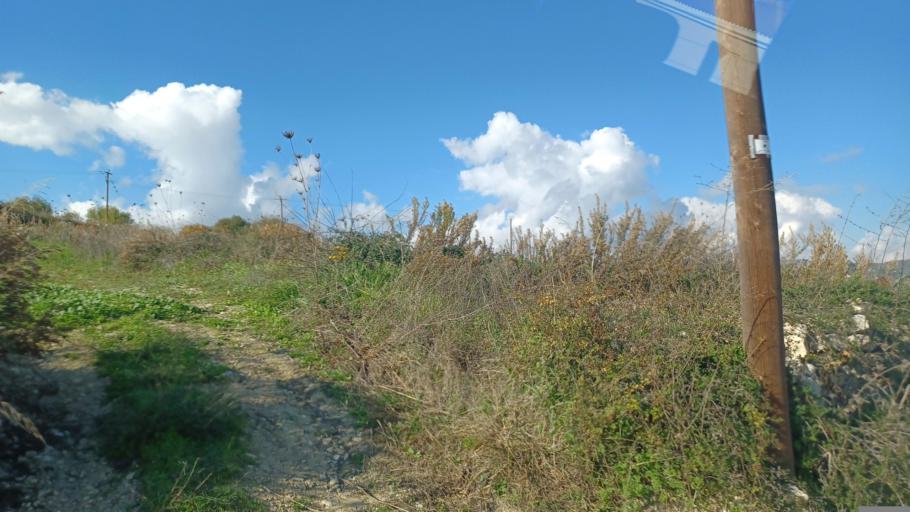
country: CY
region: Pafos
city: Mesogi
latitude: 34.8447
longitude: 32.5243
